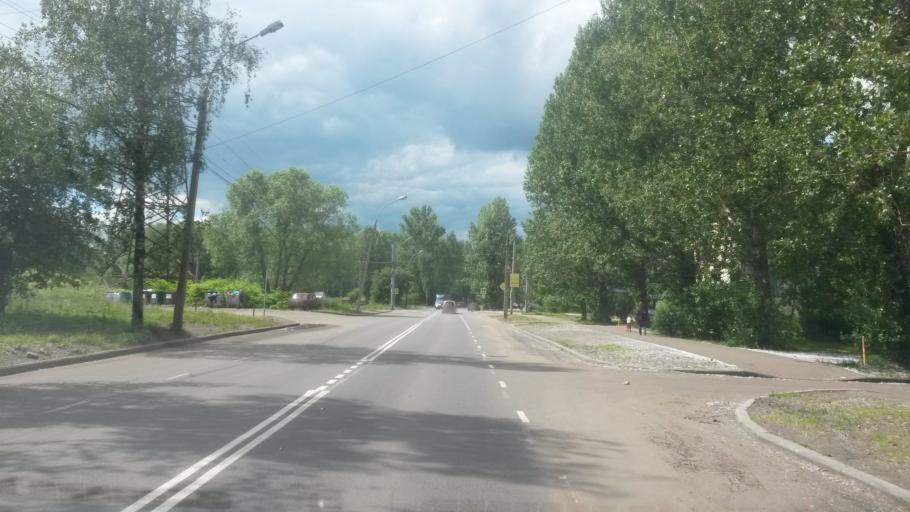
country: RU
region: Jaroslavl
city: Yaroslavl
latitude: 57.6839
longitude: 39.8123
